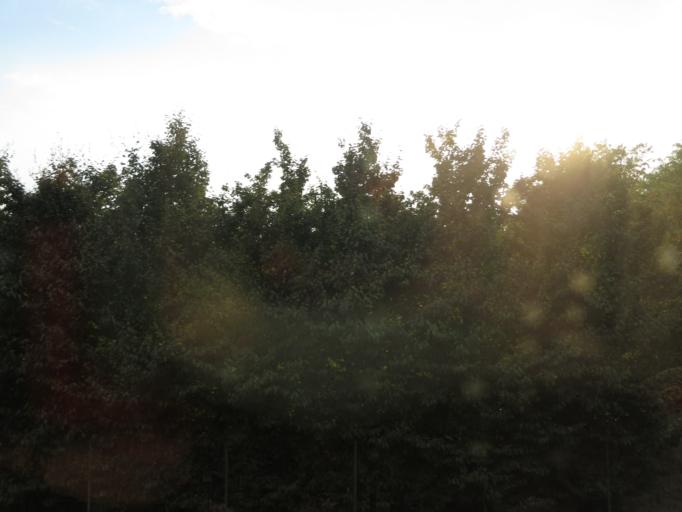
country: IT
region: Lombardy
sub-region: Provincia di Monza e Brianza
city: Lentate sul Seveso
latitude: 45.6785
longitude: 9.1278
